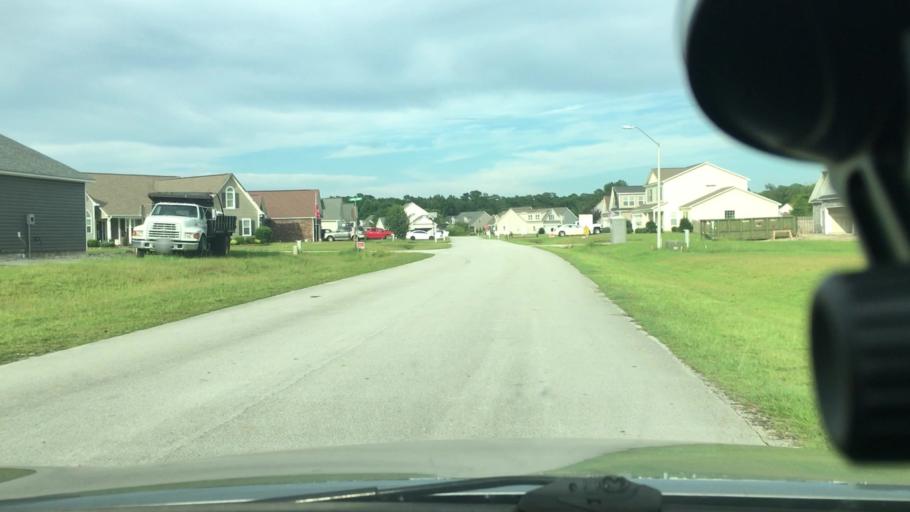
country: US
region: North Carolina
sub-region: Craven County
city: New Bern
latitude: 35.1839
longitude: -77.0577
